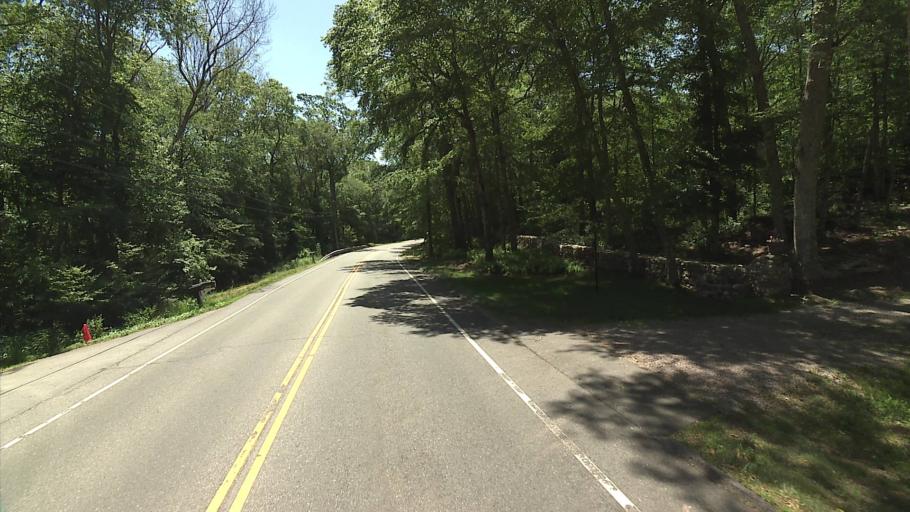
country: US
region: Rhode Island
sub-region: Washington County
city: Hopkinton
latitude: 41.4993
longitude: -71.8324
